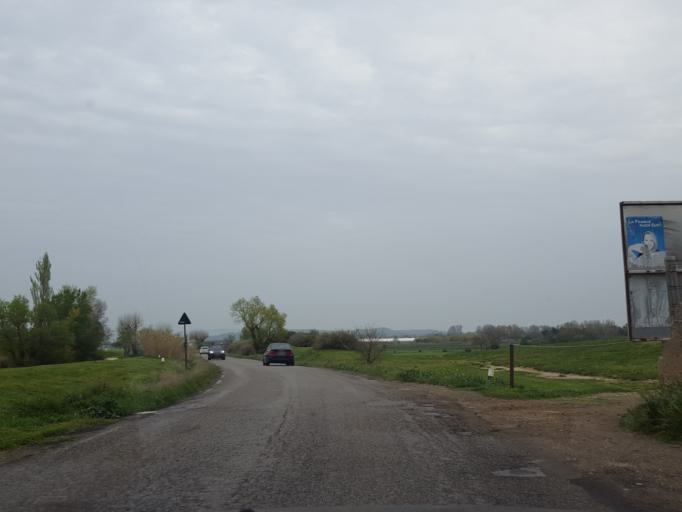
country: FR
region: Provence-Alpes-Cote d'Azur
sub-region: Departement du Vaucluse
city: Morieres-les-Avignon
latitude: 43.9199
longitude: 4.8999
